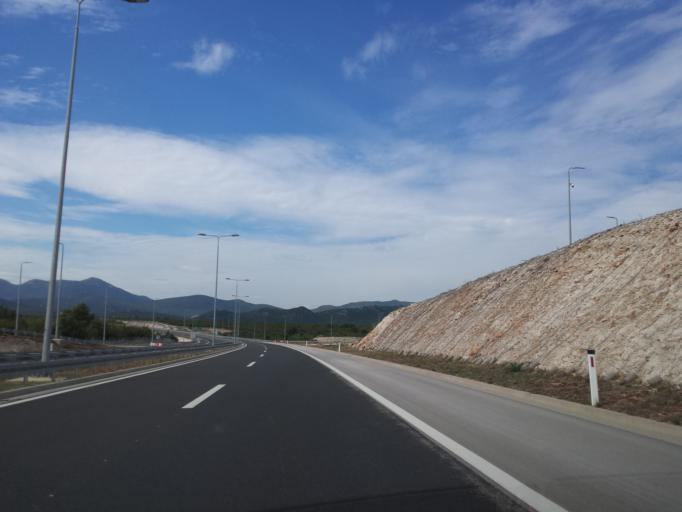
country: BA
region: Federation of Bosnia and Herzegovina
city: Ljubuski
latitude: 43.1497
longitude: 17.6025
